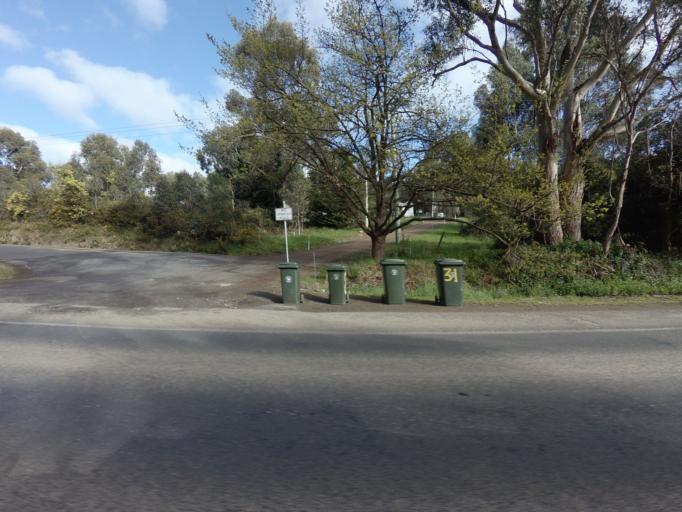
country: AU
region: Tasmania
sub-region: Huon Valley
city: Geeveston
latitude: -43.1600
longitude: 146.9524
